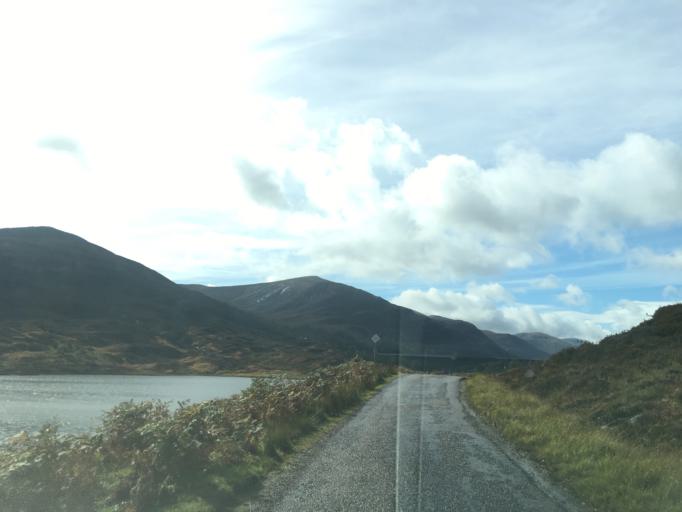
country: GB
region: Scotland
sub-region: Highland
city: Spean Bridge
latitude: 57.3437
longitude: -4.9327
